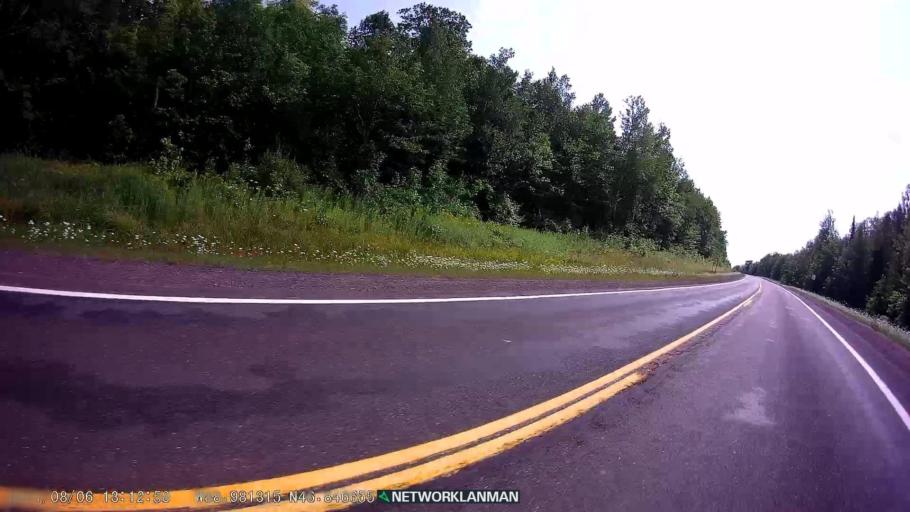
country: US
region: Michigan
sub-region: Ontonagon County
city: Ontonagon
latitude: 46.8462
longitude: -88.9819
